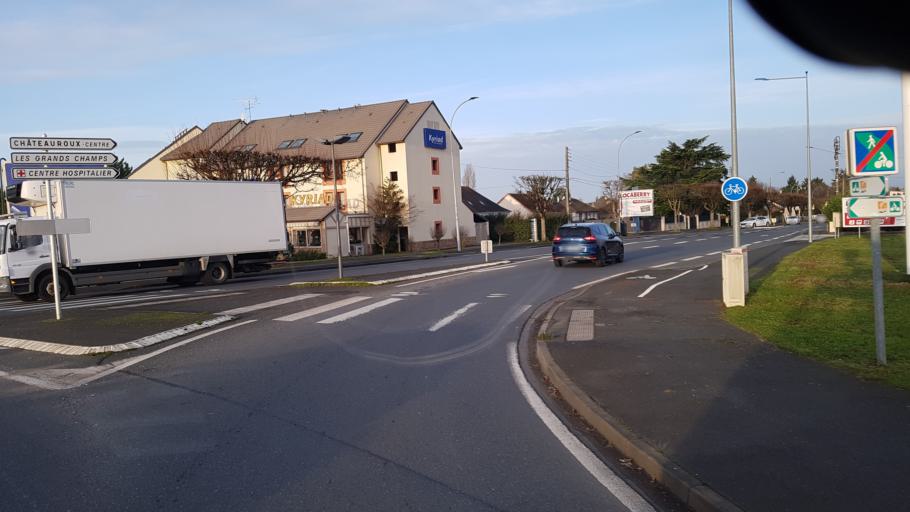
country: FR
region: Centre
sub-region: Departement de l'Indre
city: Le Poinconnet
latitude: 46.7884
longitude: 1.7034
